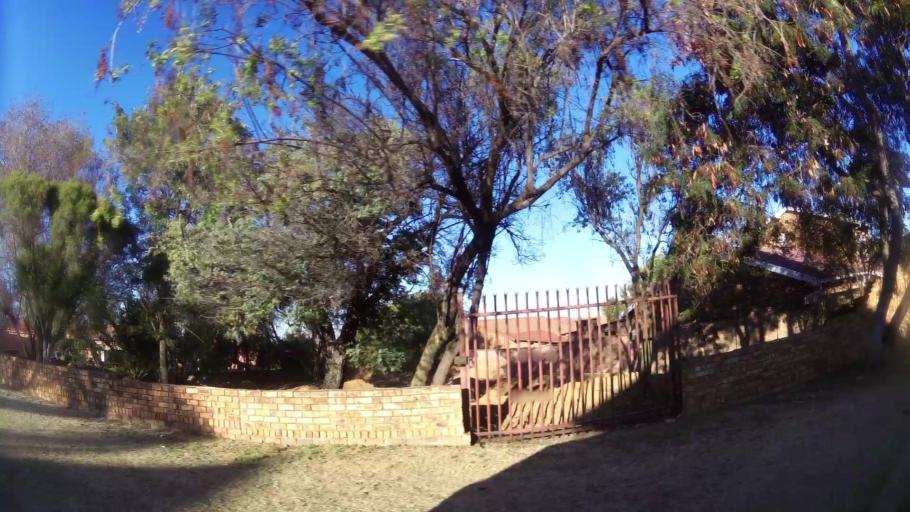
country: ZA
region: Gauteng
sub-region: City of Tshwane Metropolitan Municipality
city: Centurion
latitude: -25.9047
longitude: 28.1408
